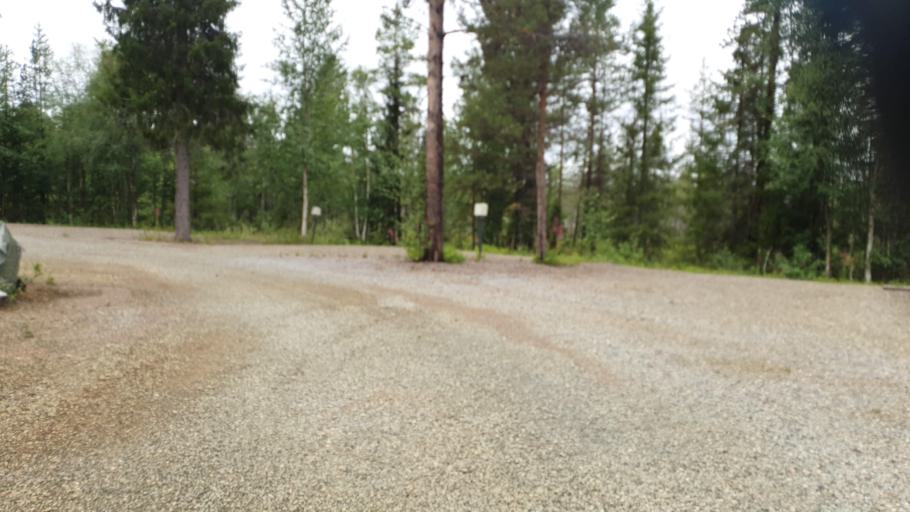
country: FI
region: Lapland
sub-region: Tunturi-Lappi
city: Kolari
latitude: 67.6136
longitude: 24.1384
